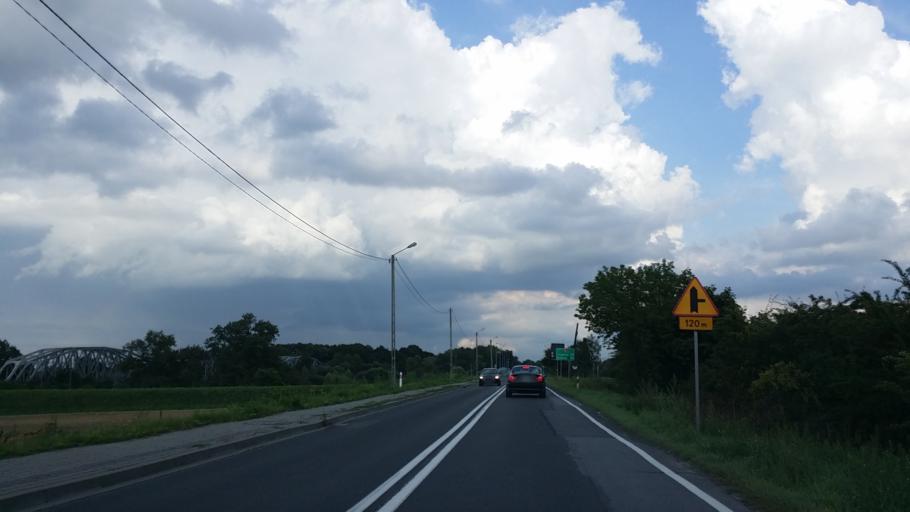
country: PL
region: Lesser Poland Voivodeship
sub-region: Powiat oswiecimski
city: Zator
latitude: 49.9987
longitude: 19.4402
